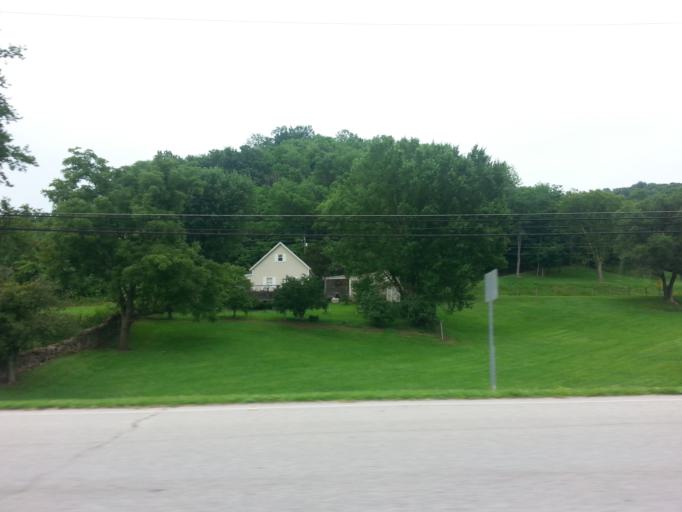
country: US
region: Ohio
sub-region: Brown County
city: Ripley
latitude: 38.7245
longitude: -83.8302
